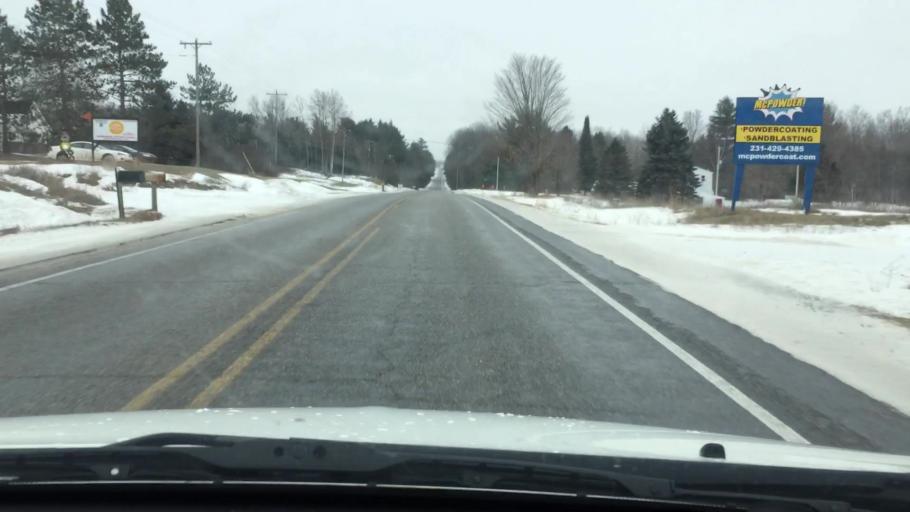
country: US
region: Michigan
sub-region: Wexford County
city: Cadillac
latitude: 44.0614
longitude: -85.4440
